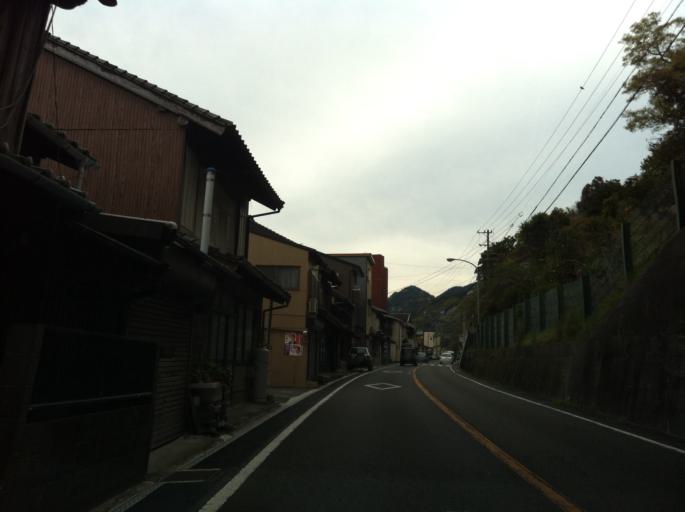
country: JP
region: Shizuoka
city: Fujinomiya
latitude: 35.0998
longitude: 138.5540
